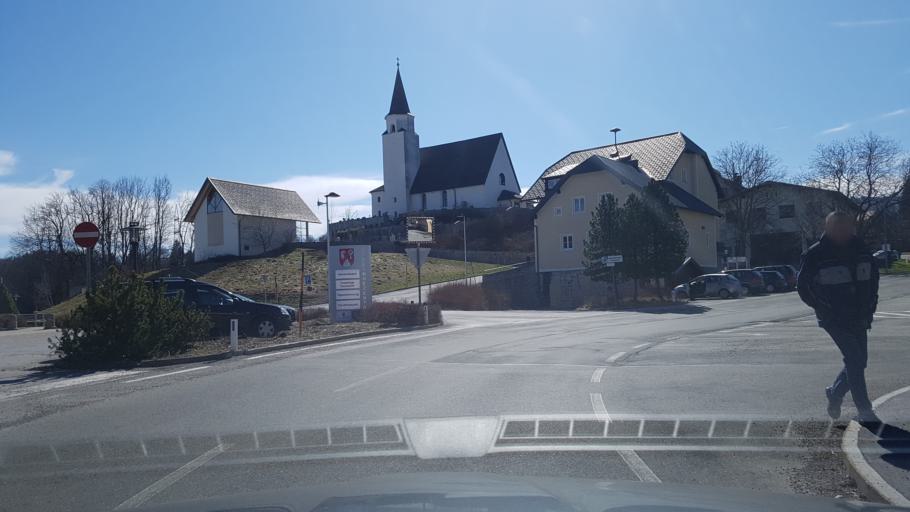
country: AT
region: Salzburg
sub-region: Politischer Bezirk Salzburg-Umgebung
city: Koppl
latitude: 47.8091
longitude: 13.1563
